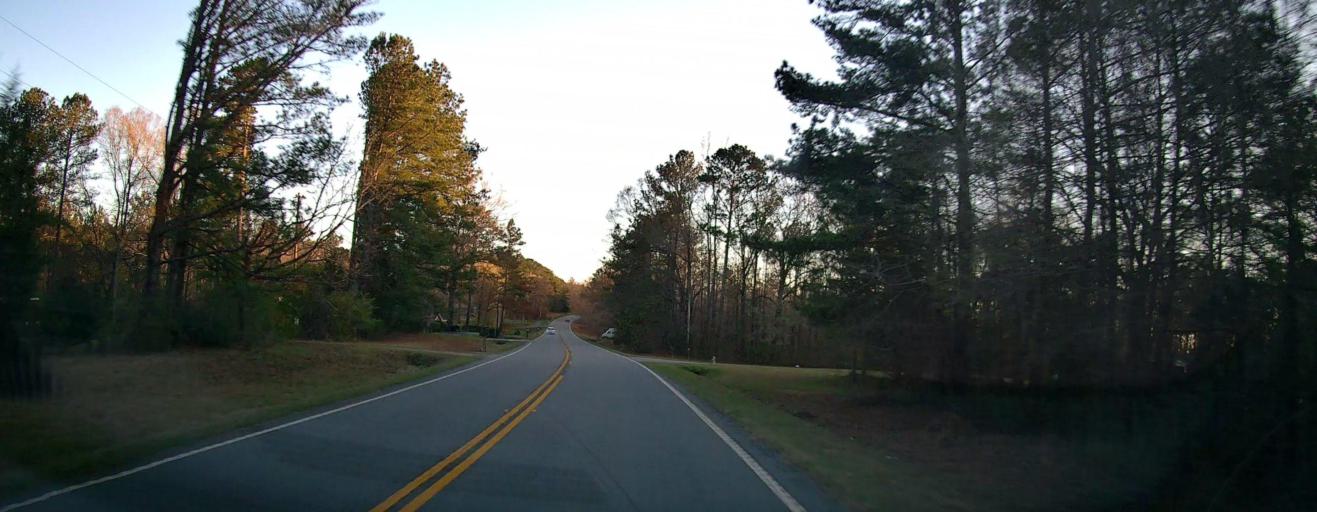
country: US
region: Alabama
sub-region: Lee County
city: Smiths Station
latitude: 32.6333
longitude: -85.0336
